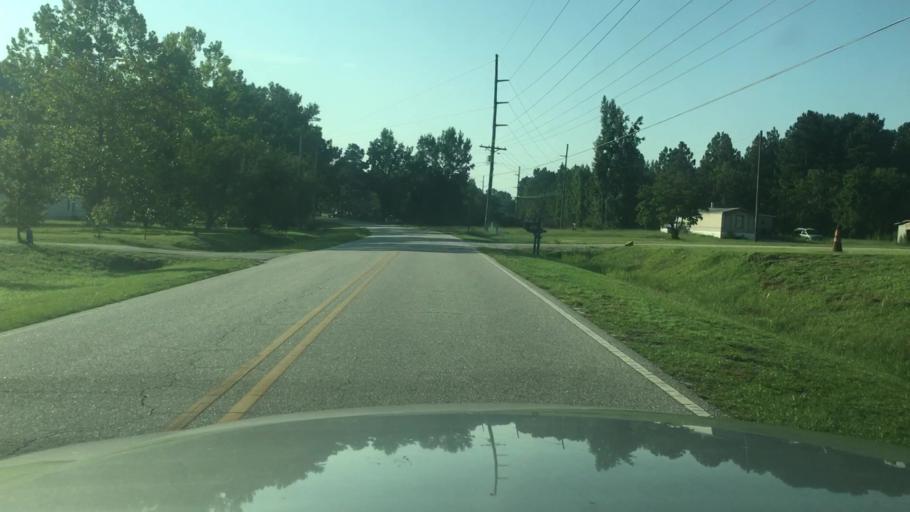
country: US
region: North Carolina
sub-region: Cumberland County
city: Spring Lake
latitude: 35.2086
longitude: -78.8936
